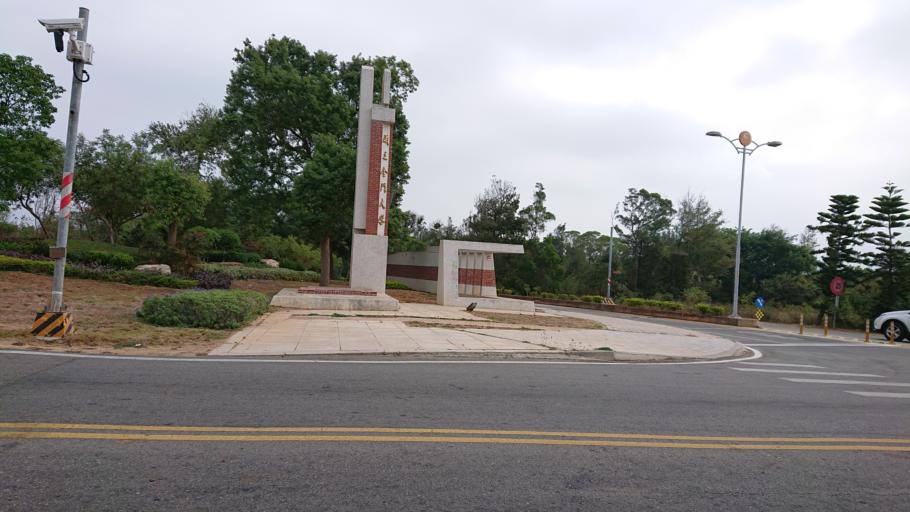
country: TW
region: Fukien
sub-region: Kinmen
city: Jincheng
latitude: 24.4445
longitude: 118.3195
